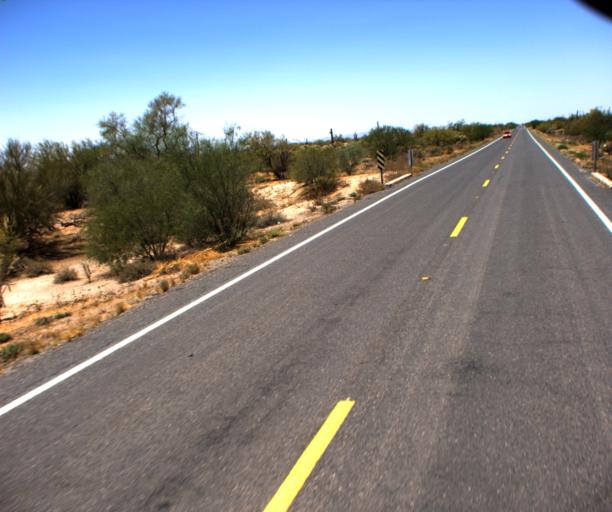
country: US
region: Arizona
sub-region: Pinal County
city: Florence
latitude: 32.8616
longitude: -111.2413
